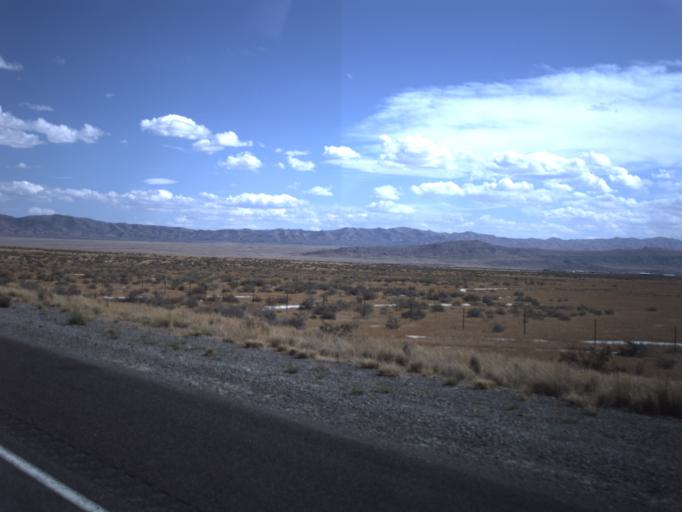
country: US
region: Utah
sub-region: Tooele County
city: Grantsville
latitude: 40.7251
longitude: -113.1424
